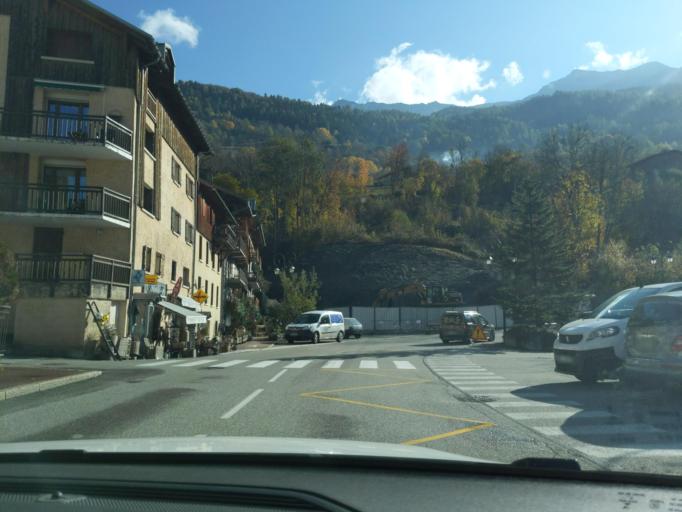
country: FR
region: Rhone-Alpes
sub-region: Departement de la Savoie
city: Seez
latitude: 45.5904
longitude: 6.8837
